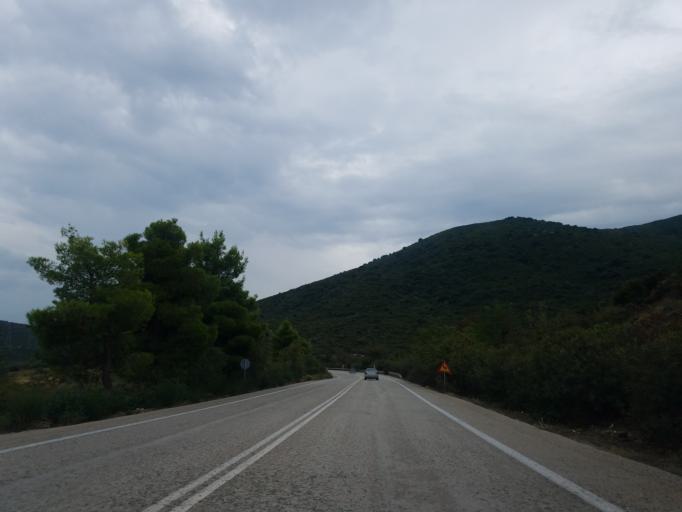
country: GR
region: Central Greece
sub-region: Nomos Voiotias
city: Livadeia
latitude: 38.4487
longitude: 22.7901
